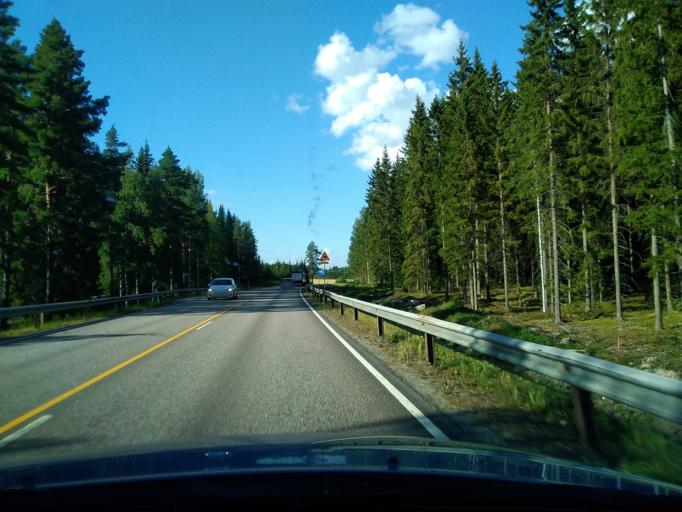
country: FI
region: Central Finland
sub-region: Keuruu
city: Keuruu
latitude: 62.1267
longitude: 24.7366
